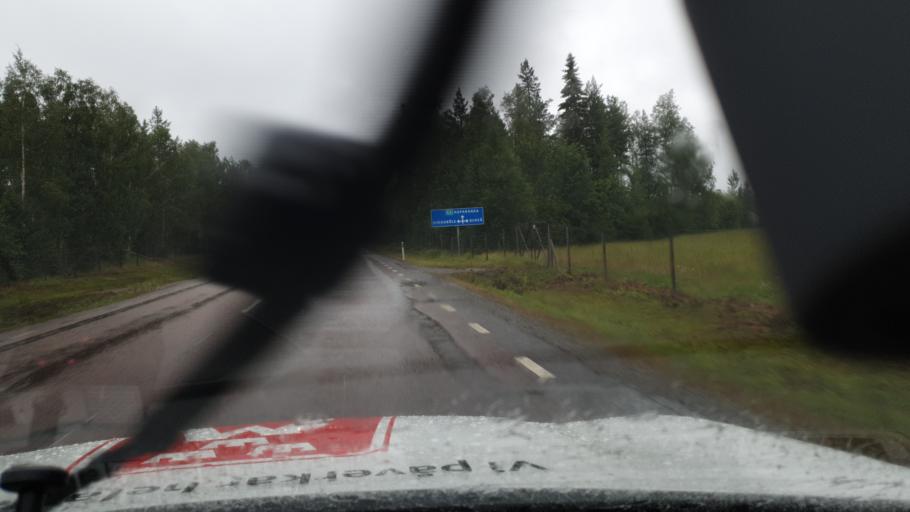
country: SE
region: Vaesterbotten
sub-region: Skelleftea Kommun
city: Burea
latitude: 64.6093
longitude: 21.1897
